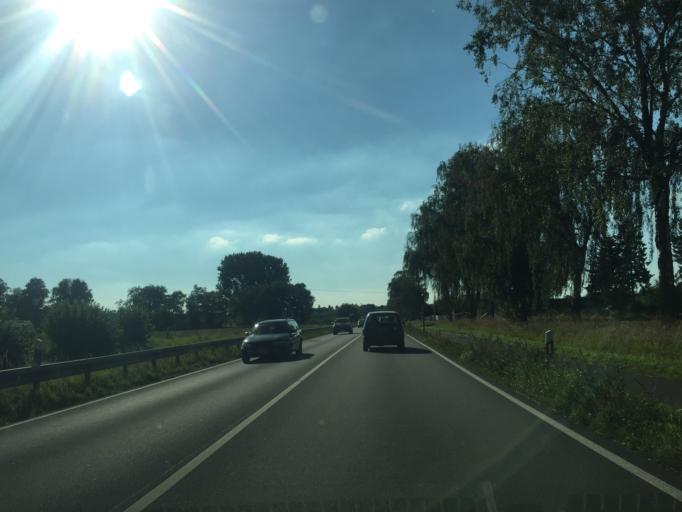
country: DE
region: North Rhine-Westphalia
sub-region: Regierungsbezirk Munster
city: Telgte
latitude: 51.9811
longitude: 7.7655
